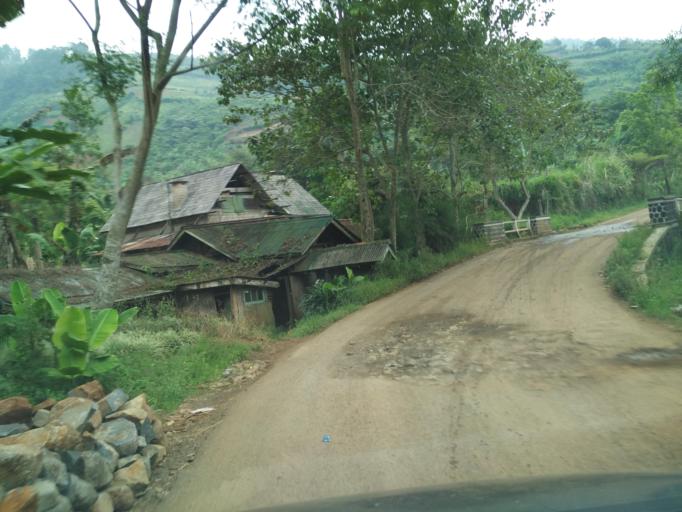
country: ID
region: West Java
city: Caringin
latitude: -6.6717
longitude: 107.0112
